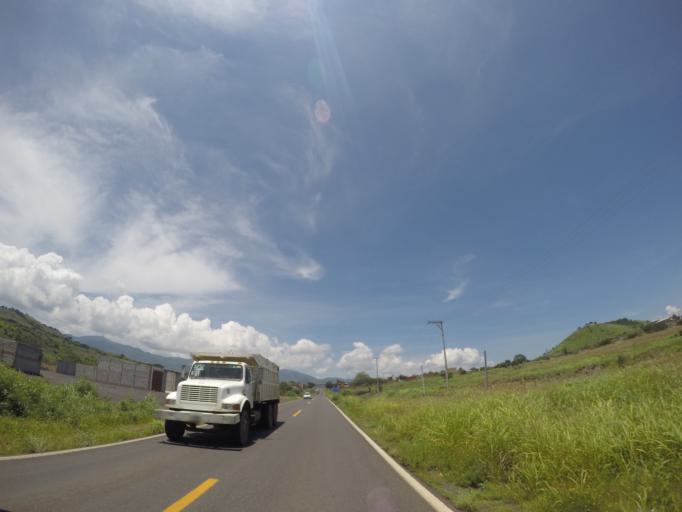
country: MX
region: Nayarit
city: Ixtlan del Rio
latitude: 21.0329
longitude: -104.3493
